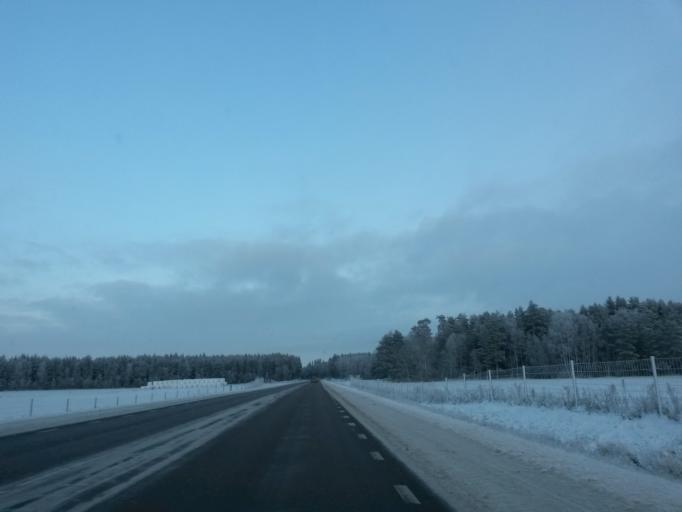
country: SE
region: Vaestra Goetaland
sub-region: Vara Kommun
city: Vara
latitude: 58.1764
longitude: 12.8922
